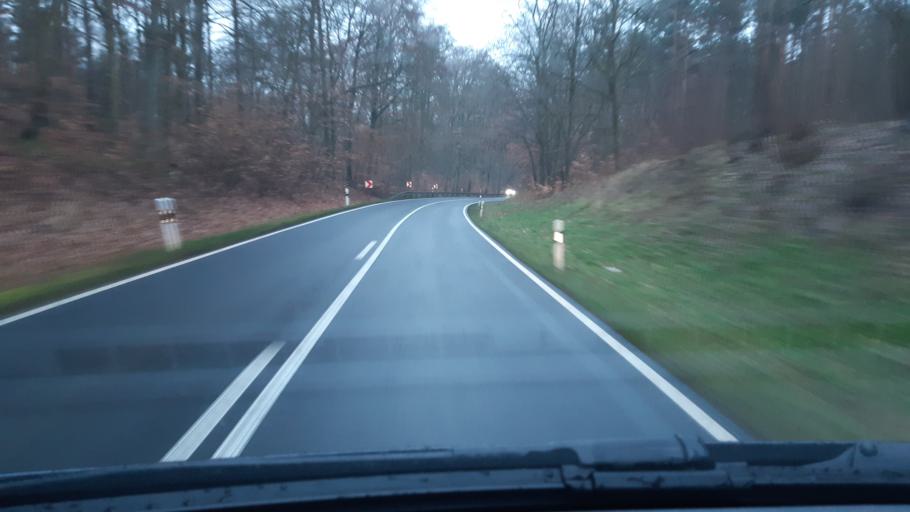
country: DE
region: Brandenburg
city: Templin
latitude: 53.1386
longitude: 13.5626
